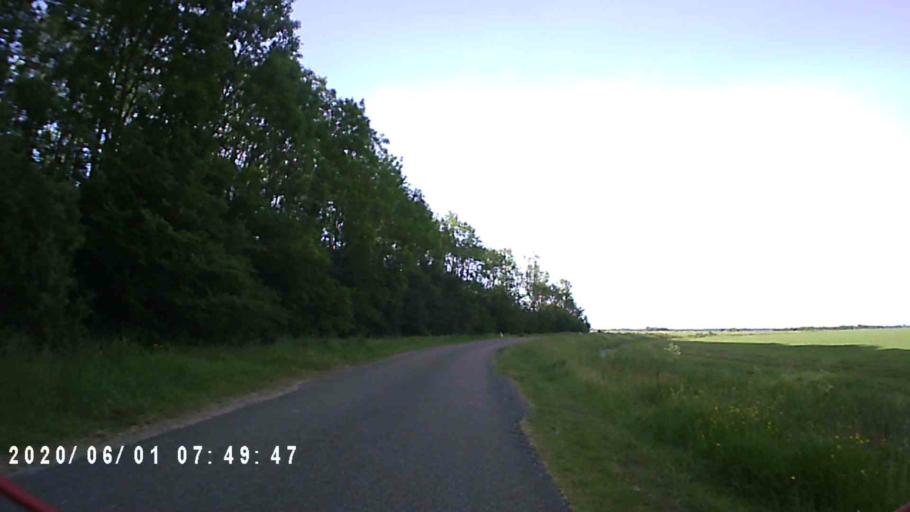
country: NL
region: Friesland
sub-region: Gemeente Dantumadiel
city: Rinsumageast
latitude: 53.2915
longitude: 5.9546
